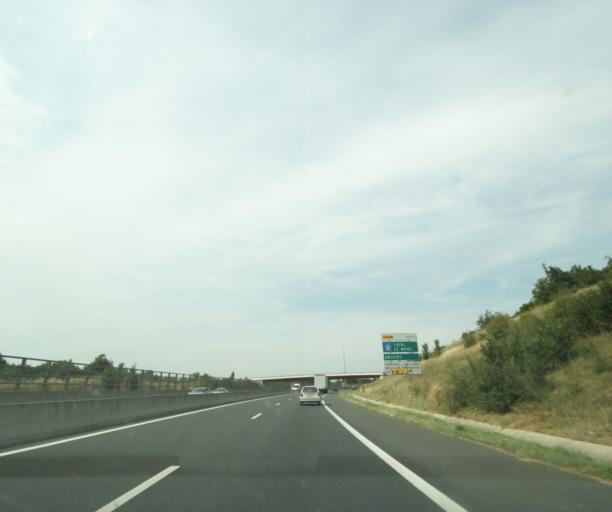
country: FR
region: Centre
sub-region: Departement d'Indre-et-Loire
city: La Membrolle-sur-Choisille
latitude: 47.4228
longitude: 0.6351
